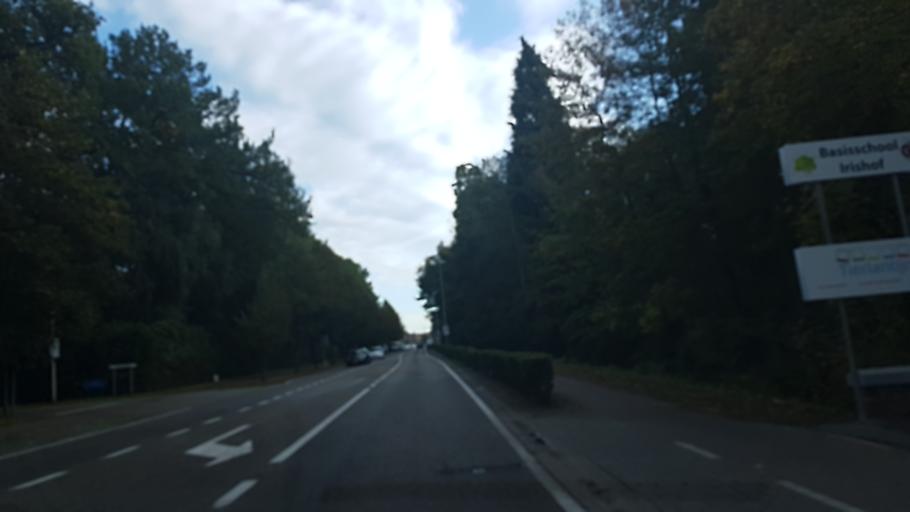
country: BE
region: Flanders
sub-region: Provincie Antwerpen
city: Kapellen
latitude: 51.3220
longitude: 4.4226
